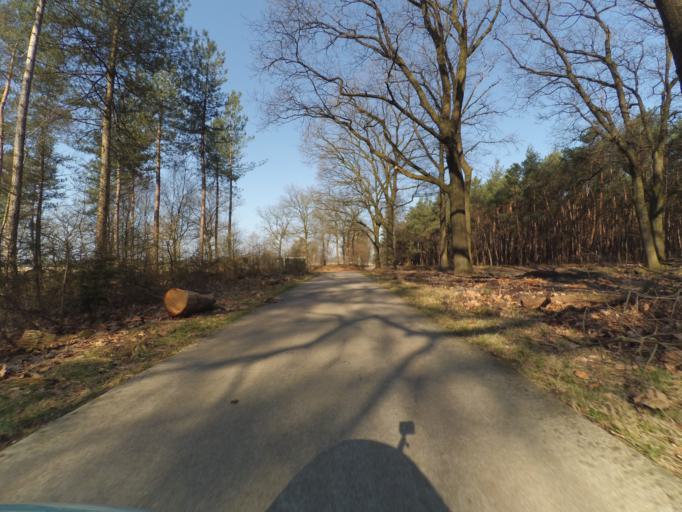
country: NL
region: Gelderland
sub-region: Gemeente Renkum
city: Oosterbeek
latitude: 52.0409
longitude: 5.8396
